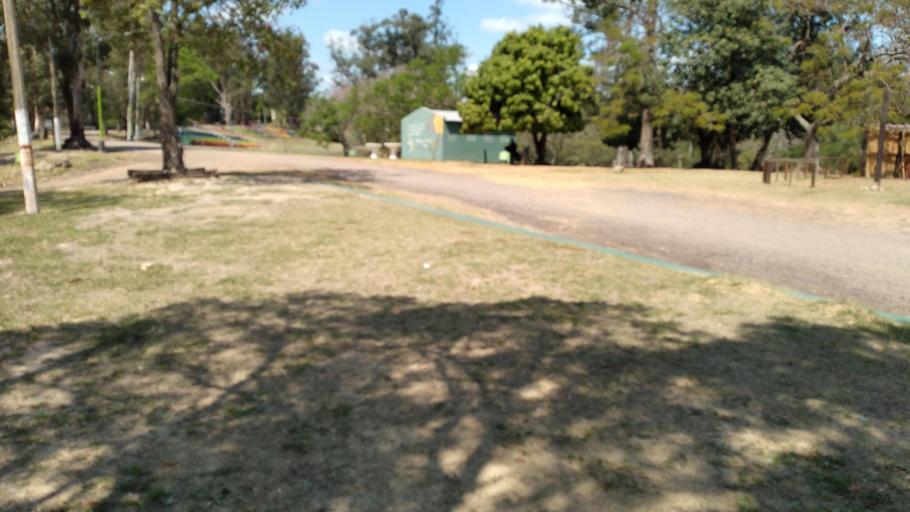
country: AR
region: Corrientes
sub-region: Departamento de Empedrado
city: Empedrado
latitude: -27.9484
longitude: -58.8133
